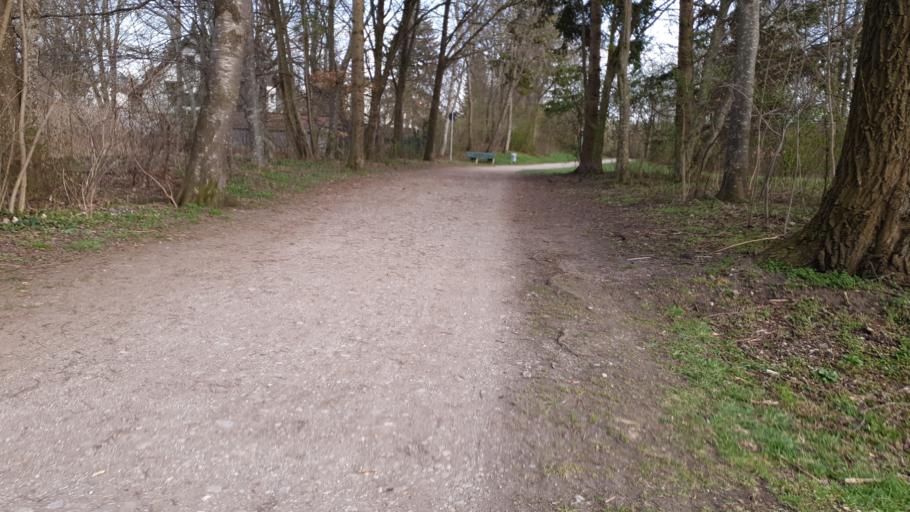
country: DE
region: Bavaria
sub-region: Upper Bavaria
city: Grobenzell
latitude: 48.1765
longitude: 11.3878
